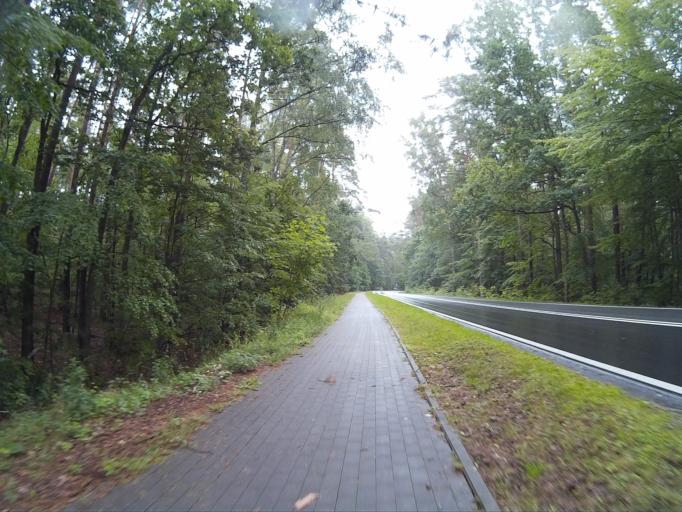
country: PL
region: Kujawsko-Pomorskie
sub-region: Powiat swiecki
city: Osie
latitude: 53.6143
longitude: 18.2823
